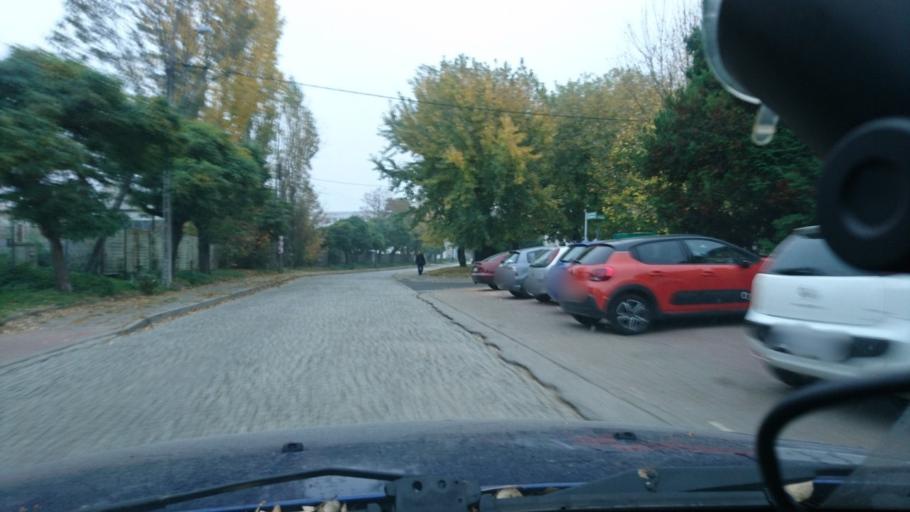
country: PL
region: Silesian Voivodeship
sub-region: Bielsko-Biala
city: Bielsko-Biala
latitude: 49.8313
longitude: 19.0574
